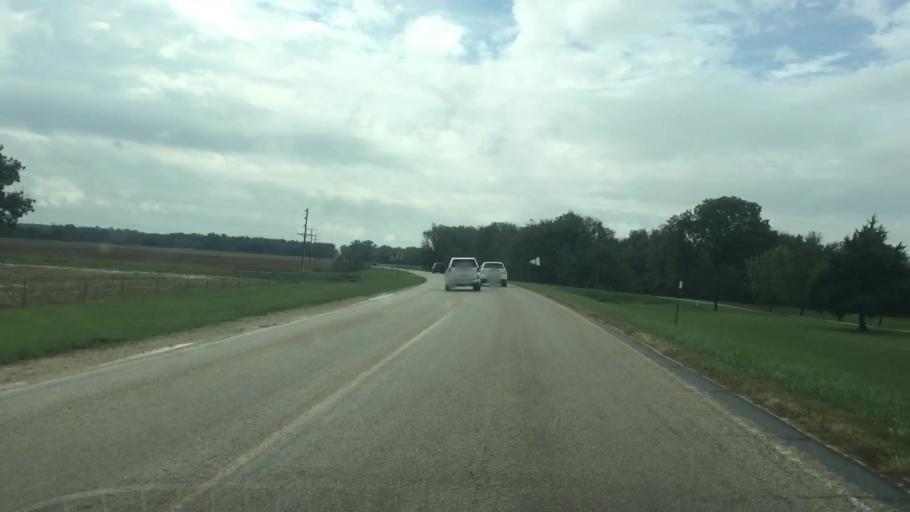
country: US
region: Kansas
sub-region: Allen County
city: Iola
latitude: 37.8794
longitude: -95.4367
